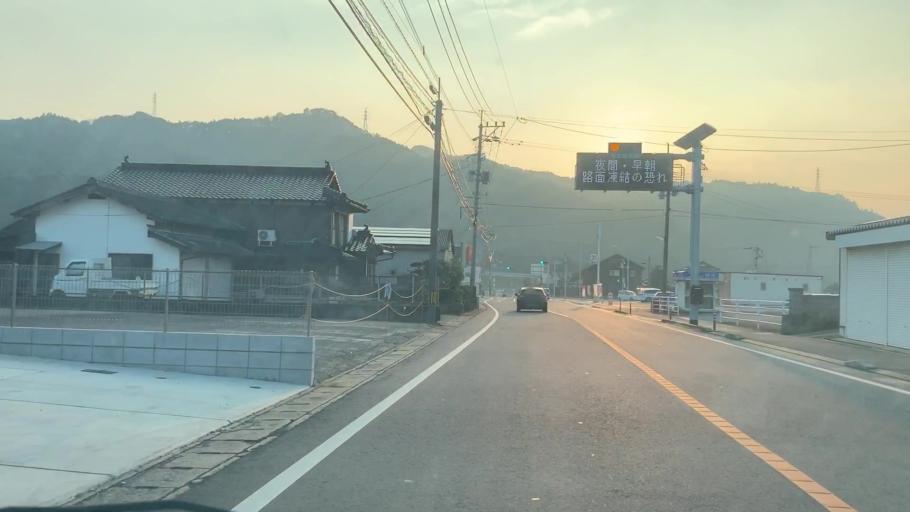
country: JP
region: Saga Prefecture
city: Takeocho-takeo
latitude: 33.2523
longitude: 129.9966
